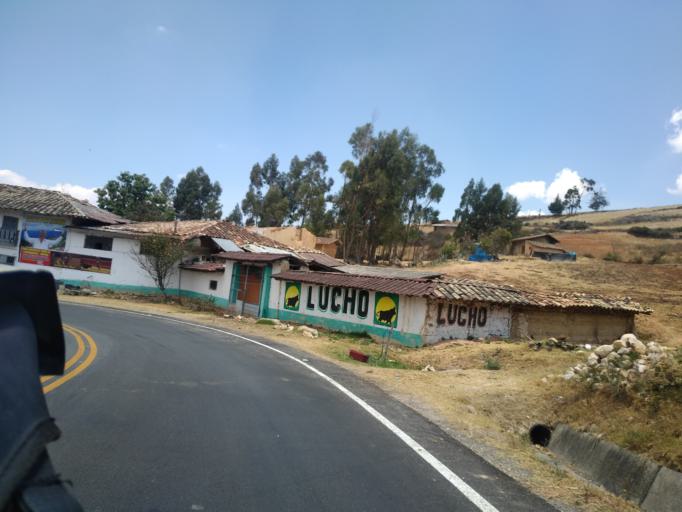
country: PE
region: Cajamarca
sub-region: San Marcos
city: San Marcos
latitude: -7.2791
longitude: -78.2414
